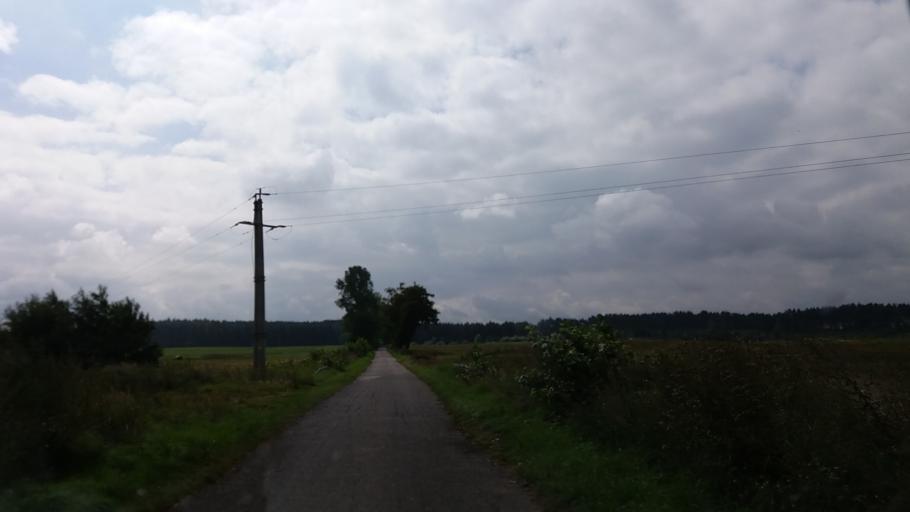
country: PL
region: West Pomeranian Voivodeship
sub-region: Powiat choszczenski
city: Krzecin
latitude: 53.0946
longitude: 15.4871
